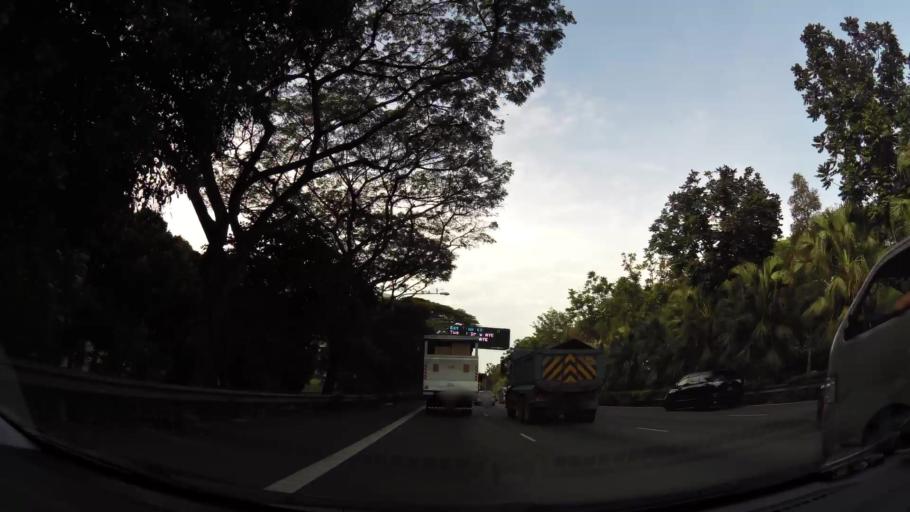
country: MY
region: Johor
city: Johor Bahru
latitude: 1.3414
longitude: 103.6847
